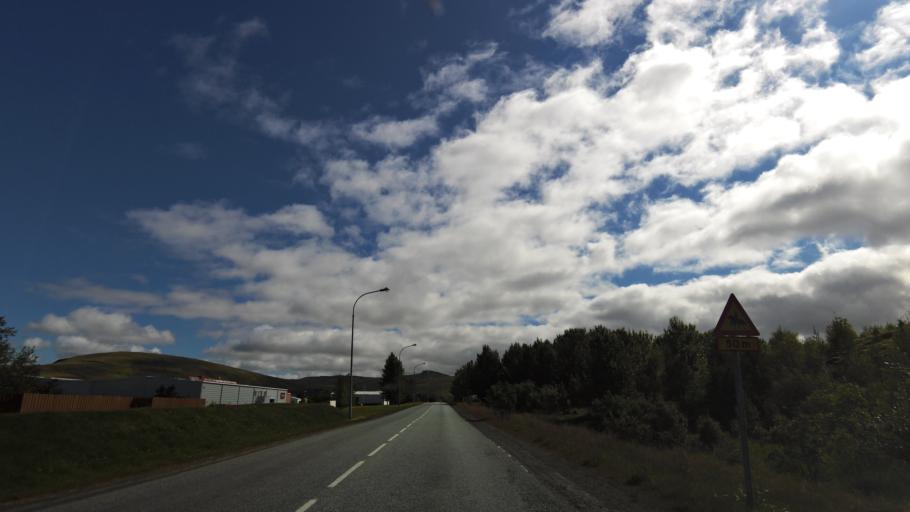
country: IS
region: Capital Region
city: Mosfellsbaer
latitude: 64.1622
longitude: -21.6847
